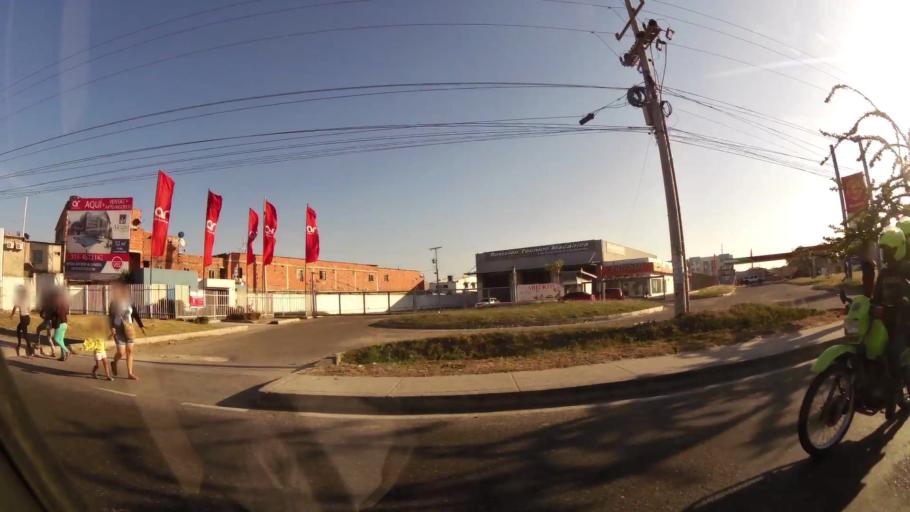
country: CO
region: Atlantico
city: Soledad
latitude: 10.9242
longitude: -74.7930
